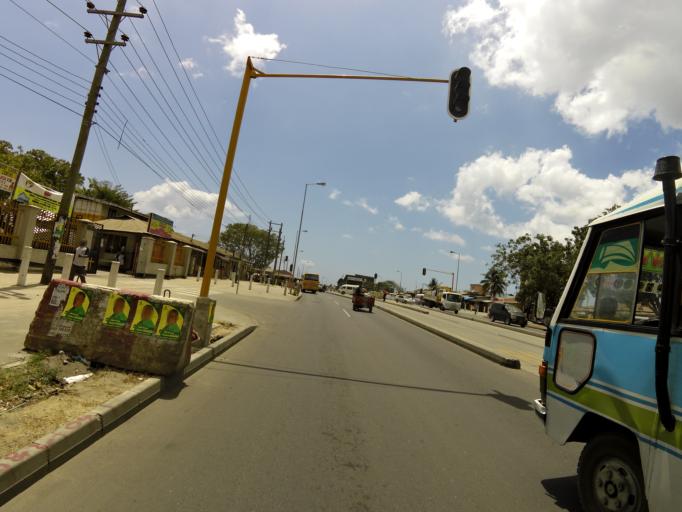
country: TZ
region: Dar es Salaam
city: Magomeni
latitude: -6.8046
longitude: 39.2595
